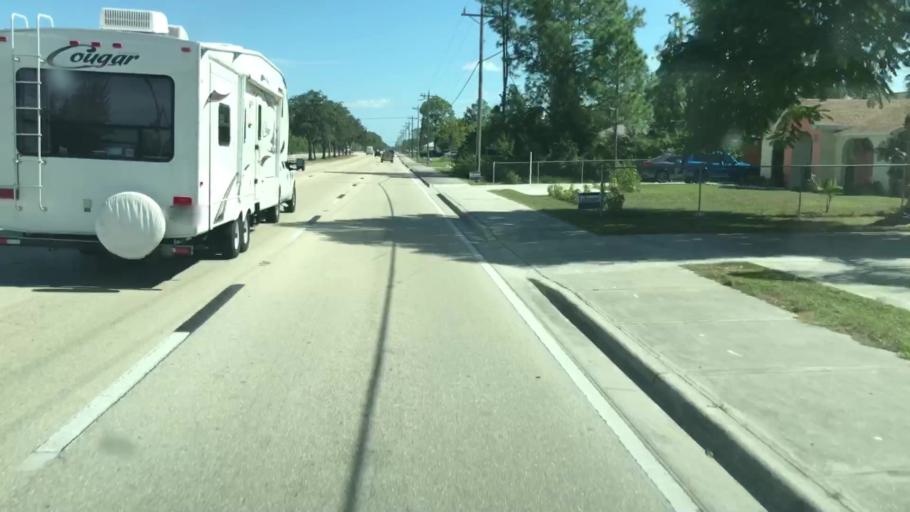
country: US
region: Florida
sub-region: Lee County
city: Gateway
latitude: 26.6169
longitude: -81.7049
